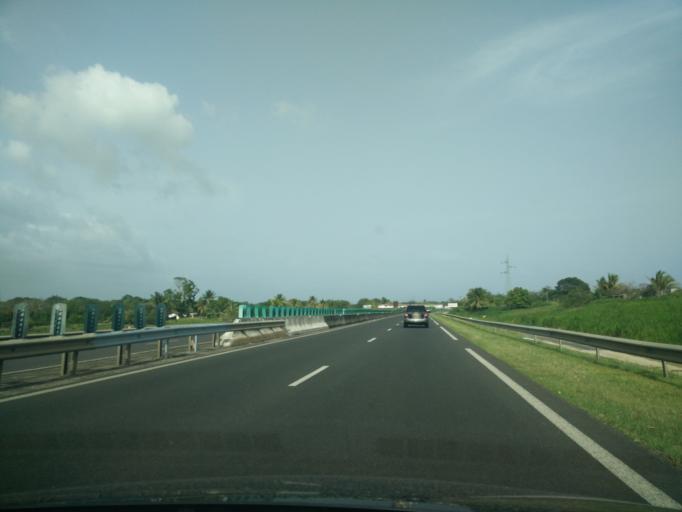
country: GP
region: Guadeloupe
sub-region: Guadeloupe
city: Petit-Bourg
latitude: 16.1815
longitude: -61.6014
